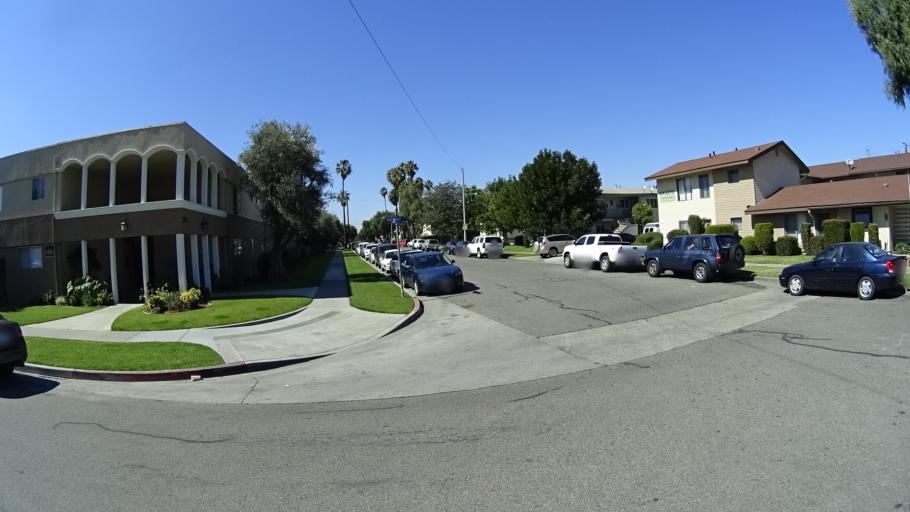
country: US
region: California
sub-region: Orange County
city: Garden Grove
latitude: 33.8045
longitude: -117.9446
